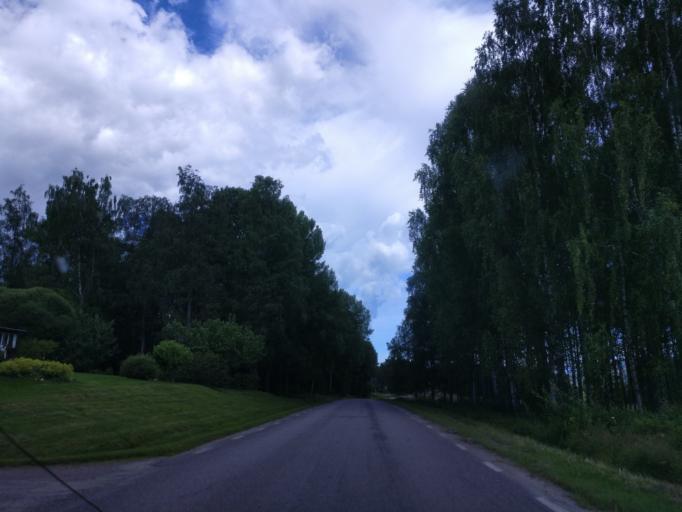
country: SE
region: Vaermland
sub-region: Hagfors Kommun
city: Ekshaerad
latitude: 60.1332
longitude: 13.4580
